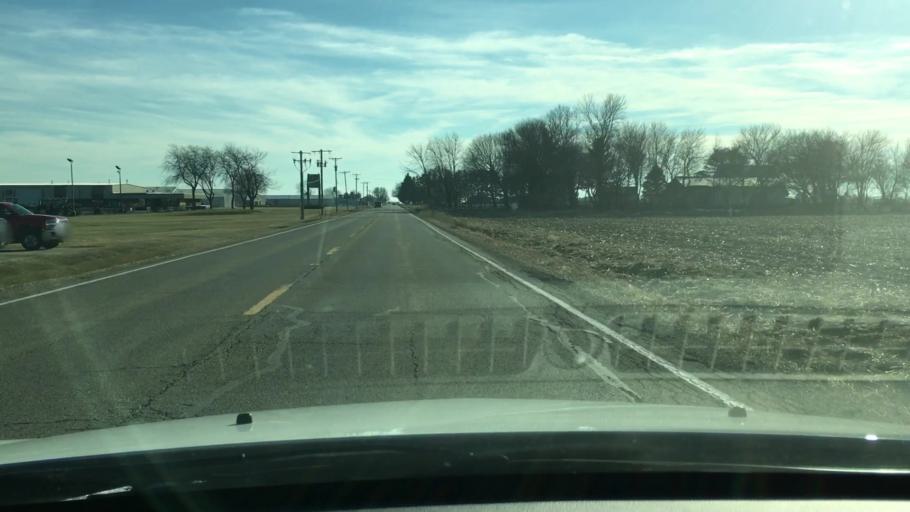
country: US
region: Illinois
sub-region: LaSalle County
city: Mendota
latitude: 41.5246
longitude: -89.1275
